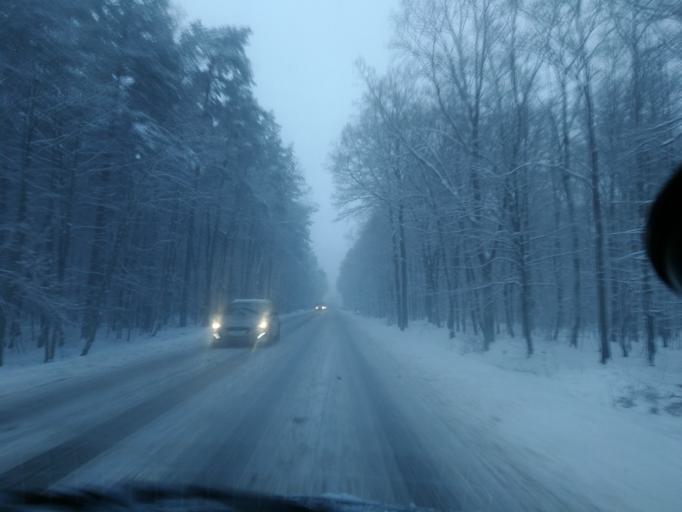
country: PL
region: Silesian Voivodeship
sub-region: Powiat pszczynski
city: Kryry
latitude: 50.0229
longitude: 18.8415
